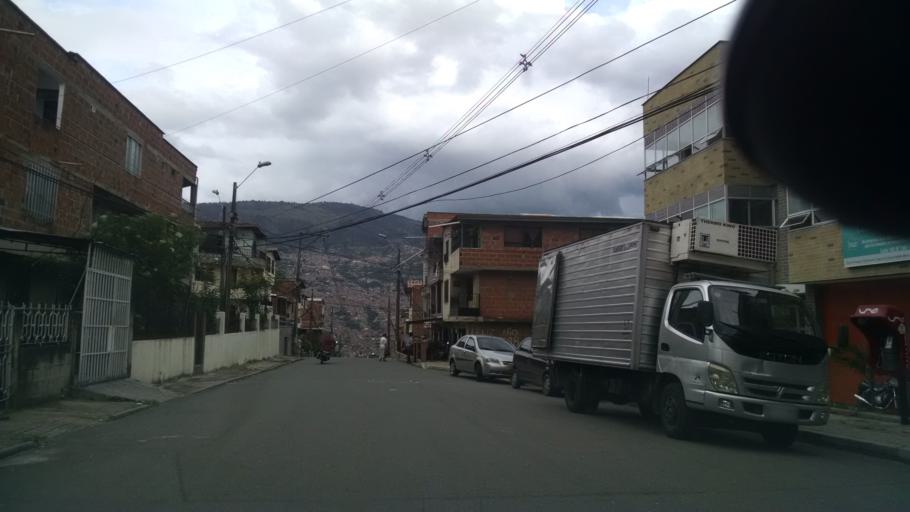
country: CO
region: Antioquia
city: Bello
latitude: 6.3009
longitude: -75.5742
